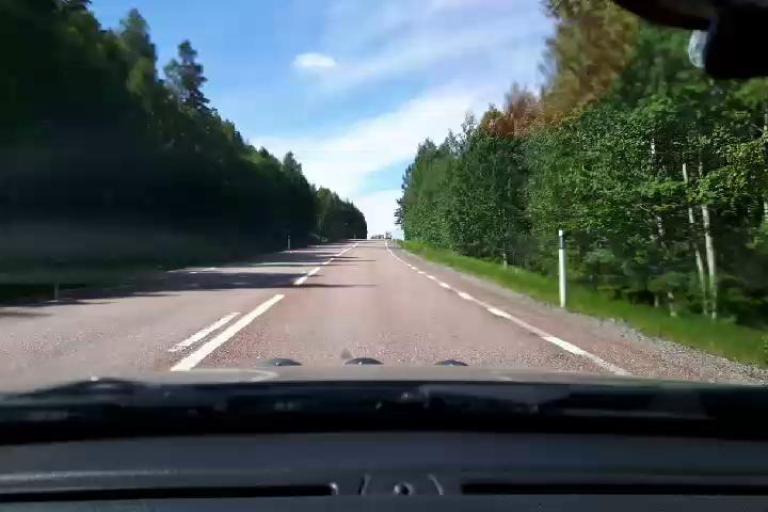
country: SE
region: Gaevleborg
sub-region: Bollnas Kommun
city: Kilafors
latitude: 61.1982
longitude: 16.7620
